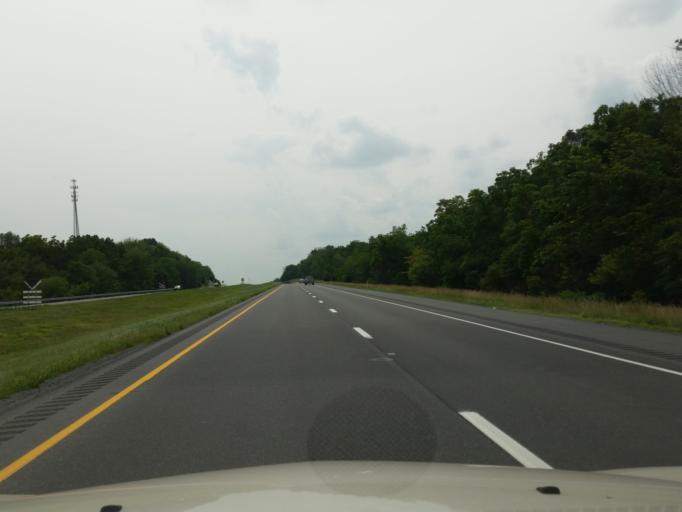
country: US
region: Pennsylvania
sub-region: Juniata County
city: Mifflintown
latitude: 40.5443
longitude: -77.3233
